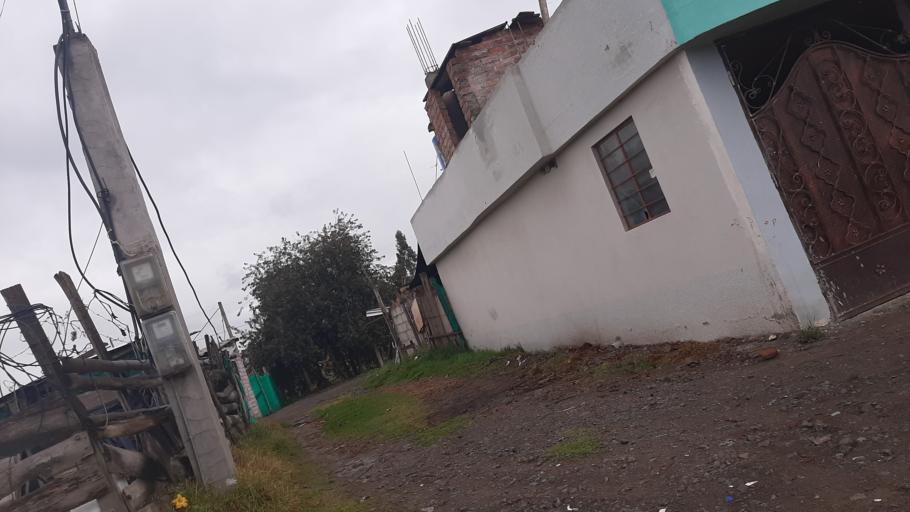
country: EC
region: Chimborazo
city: Riobamba
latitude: -1.6502
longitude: -78.6354
